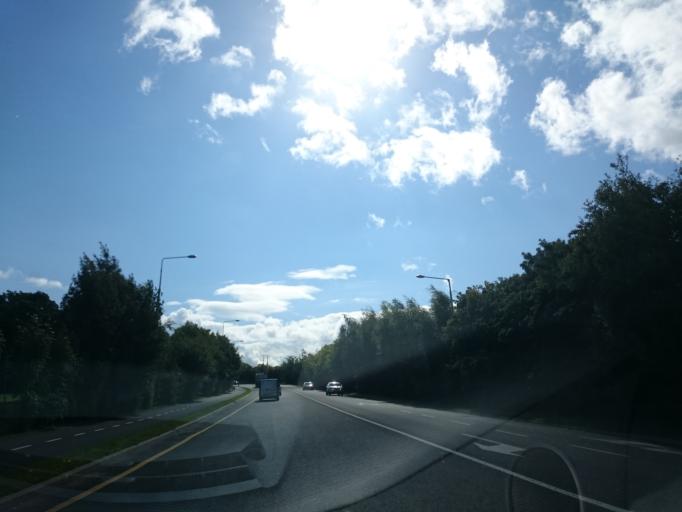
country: IE
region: Leinster
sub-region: Kilkenny
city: Kilkenny
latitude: 52.6376
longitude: -7.2568
